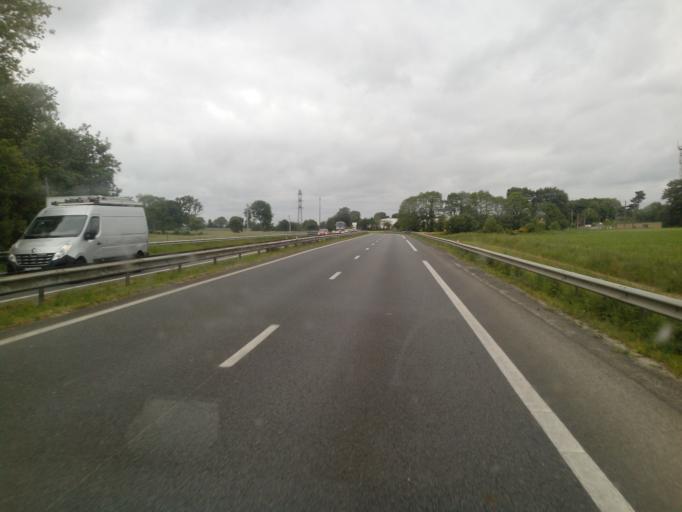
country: FR
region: Brittany
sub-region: Departement des Cotes-d'Armor
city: Graces
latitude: 48.5613
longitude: -3.1860
